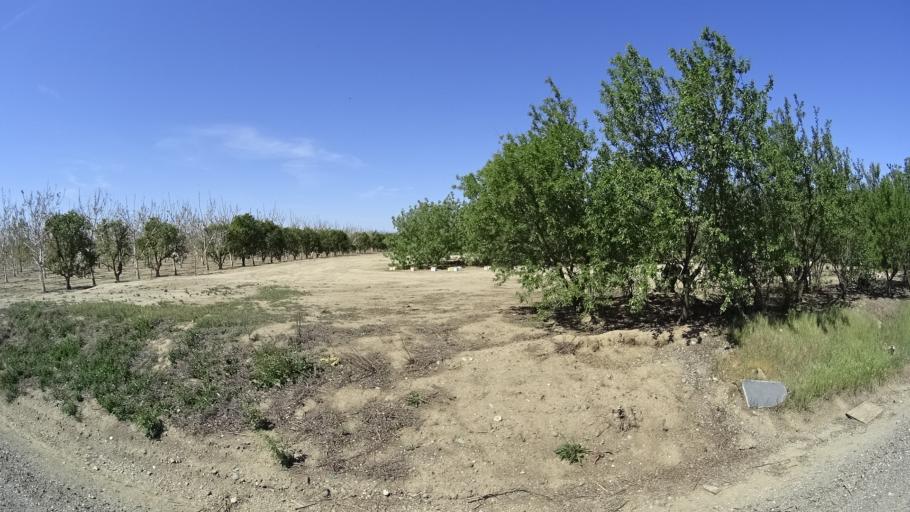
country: US
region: California
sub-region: Glenn County
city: Orland
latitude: 39.7054
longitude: -122.1407
